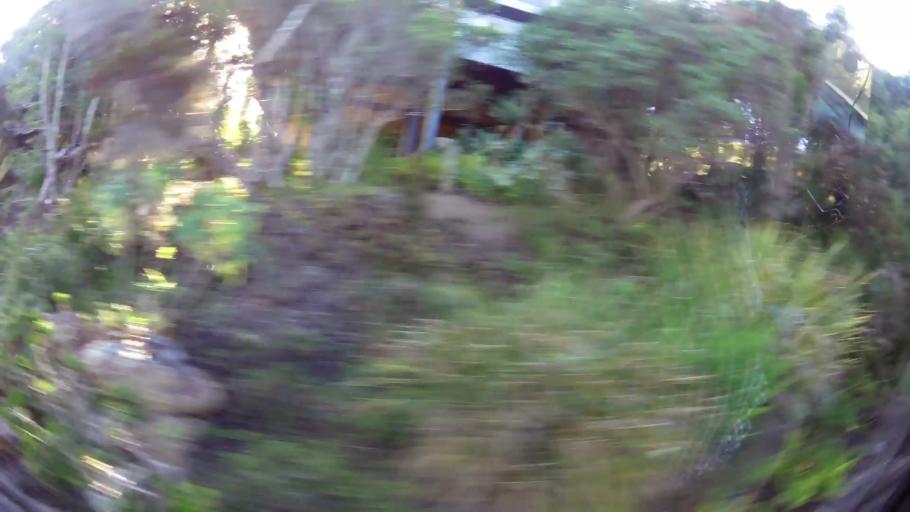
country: ZA
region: Western Cape
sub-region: Eden District Municipality
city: George
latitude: -33.9901
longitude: 22.5855
